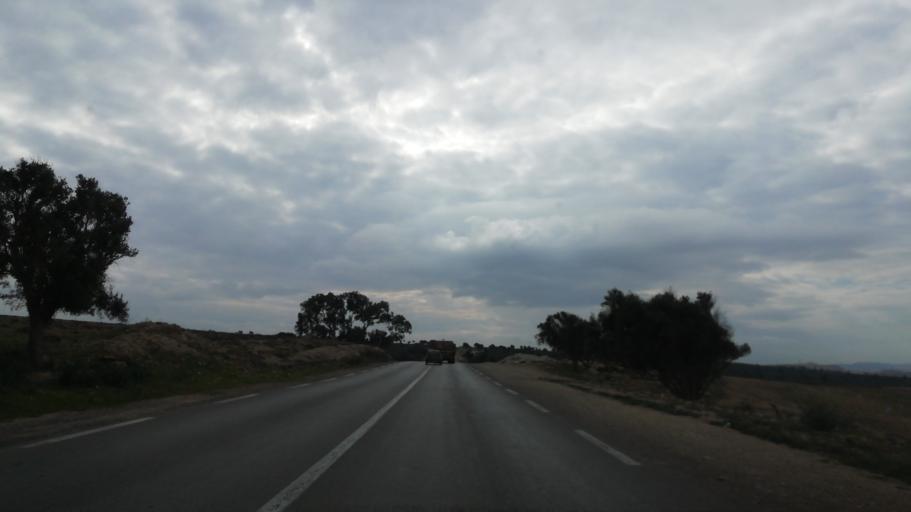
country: DZ
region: Oran
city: Ain el Bya
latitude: 35.7344
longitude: -0.3552
